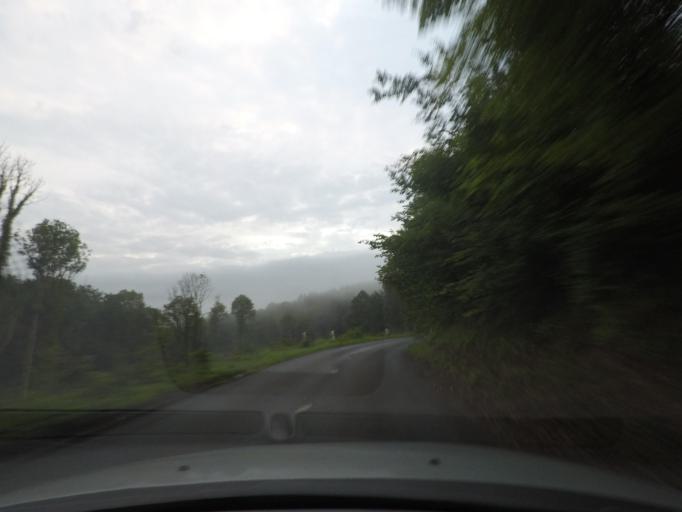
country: FR
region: Haute-Normandie
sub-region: Departement de la Seine-Maritime
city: Fontaine-le-Bourg
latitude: 49.5500
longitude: 1.1195
